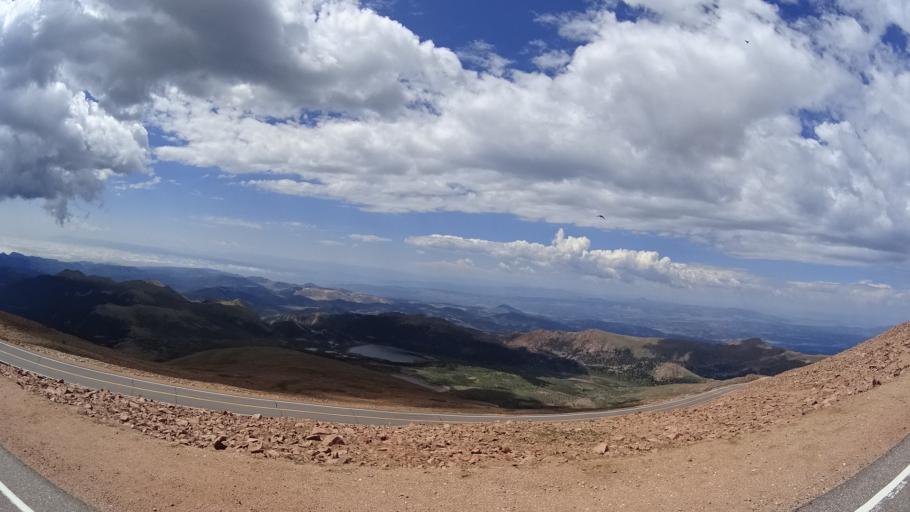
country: US
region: Colorado
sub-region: El Paso County
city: Cascade-Chipita Park
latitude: 38.8378
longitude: -105.0438
